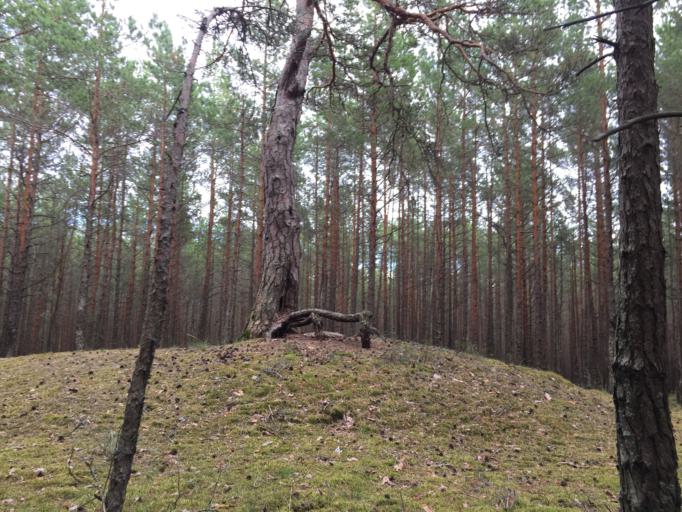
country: LV
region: Riga
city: Jaunciems
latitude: 57.1039
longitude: 24.1761
